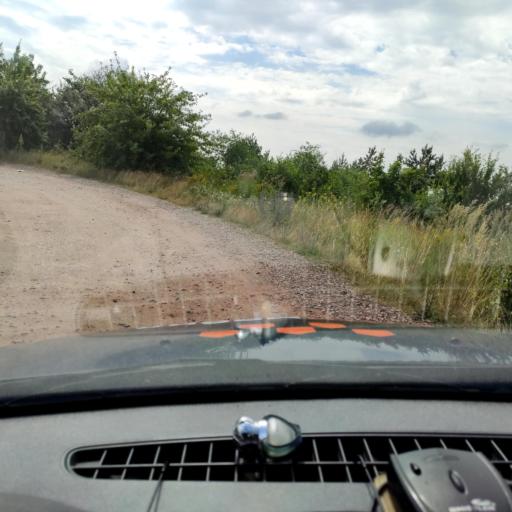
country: RU
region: Voronezj
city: Ramon'
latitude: 52.0714
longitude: 39.3232
